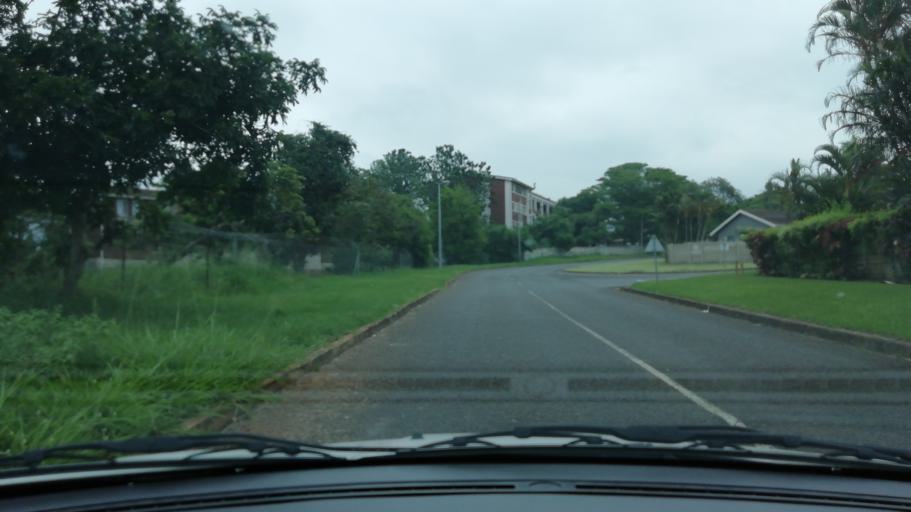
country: ZA
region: KwaZulu-Natal
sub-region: uThungulu District Municipality
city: Empangeni
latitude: -28.7395
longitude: 31.9006
